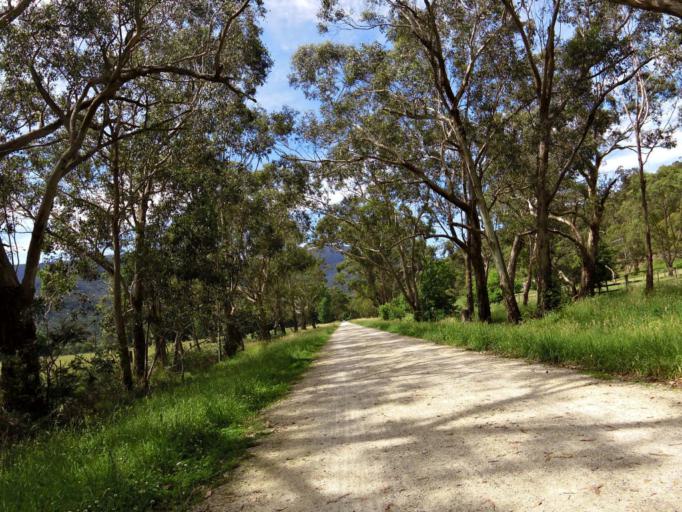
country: AU
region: Victoria
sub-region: Yarra Ranges
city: Millgrove
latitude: -37.7600
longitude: 145.6464
